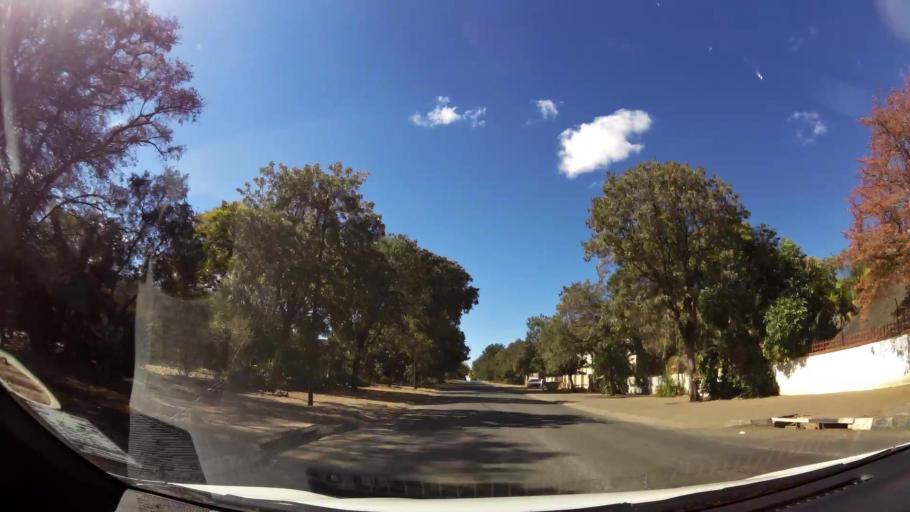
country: ZA
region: Limpopo
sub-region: Capricorn District Municipality
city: Polokwane
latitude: -23.9140
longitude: 29.4631
